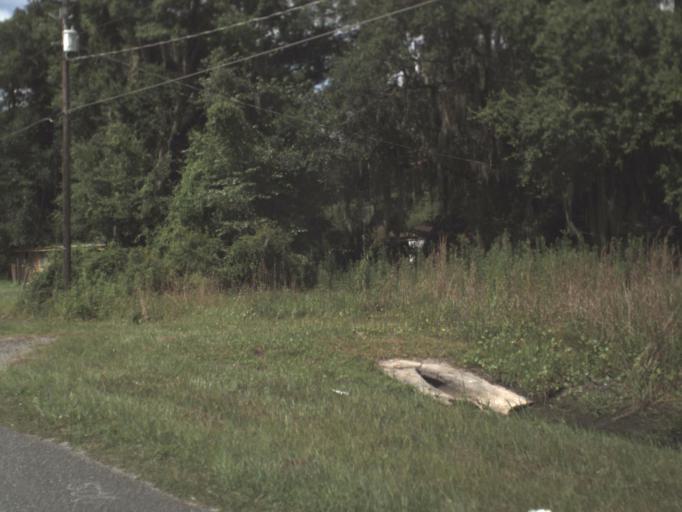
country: US
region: Florida
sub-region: Columbia County
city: Five Points
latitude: 30.2467
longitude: -82.6384
